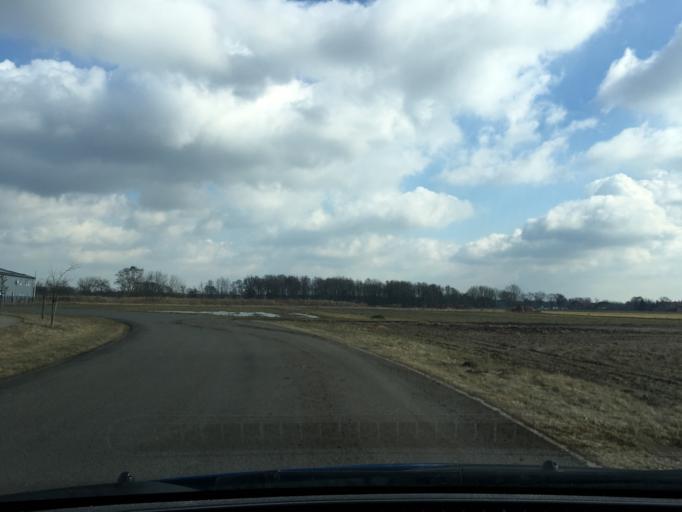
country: DE
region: Lower Saxony
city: Wittorf
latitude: 53.3143
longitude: 10.3720
